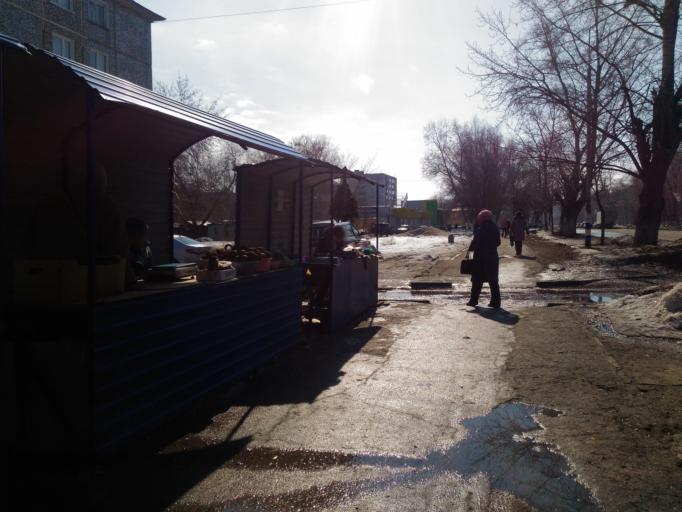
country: RU
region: Ulyanovsk
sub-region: Ulyanovskiy Rayon
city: Ulyanovsk
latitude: 54.3294
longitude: 48.4835
